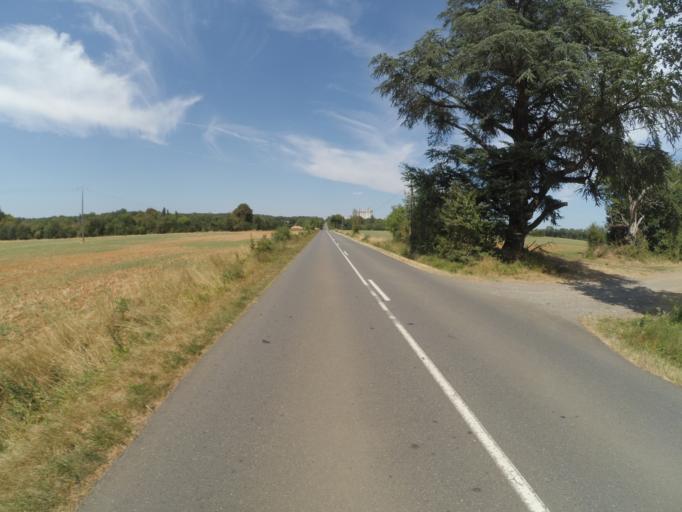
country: FR
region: Poitou-Charentes
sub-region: Departement de la Vienne
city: Usson-du-Poitou
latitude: 46.2646
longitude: 0.5212
